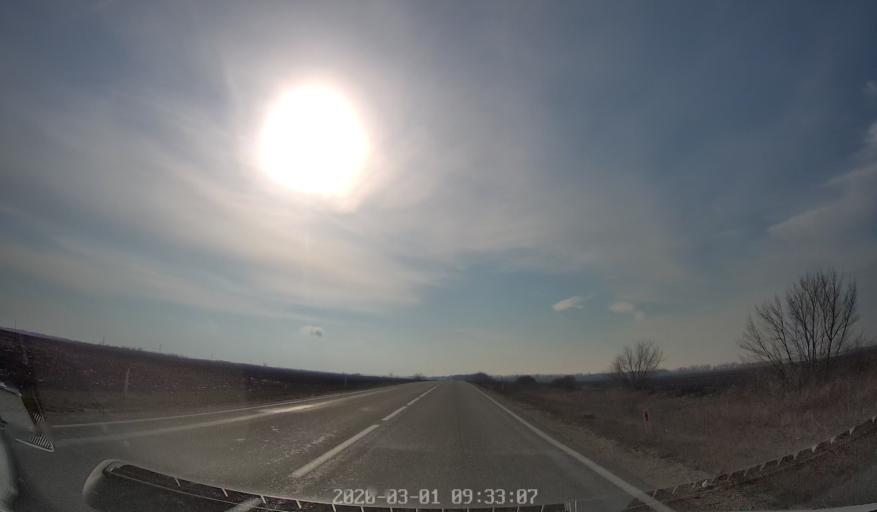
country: MD
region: Causeni
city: Causeni
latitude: 46.6237
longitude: 29.4706
